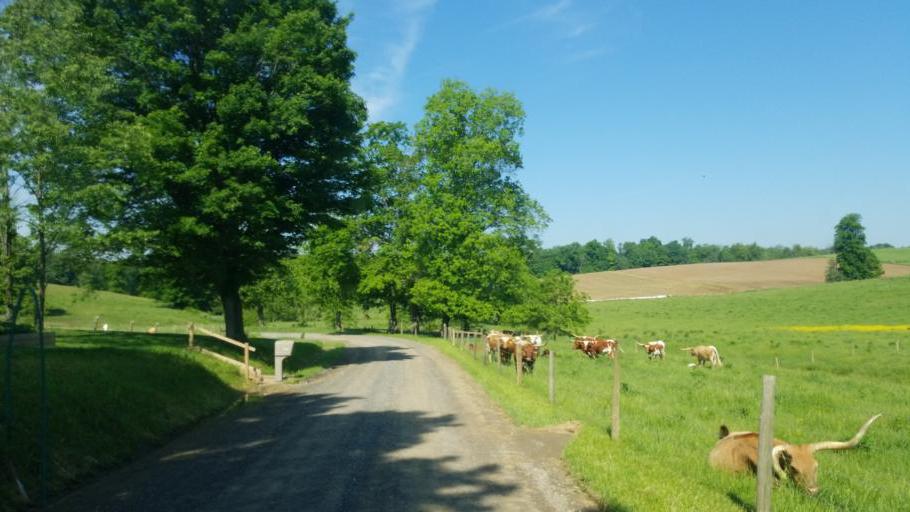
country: US
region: Ohio
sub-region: Tuscarawas County
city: Sugarcreek
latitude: 40.4632
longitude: -81.7587
